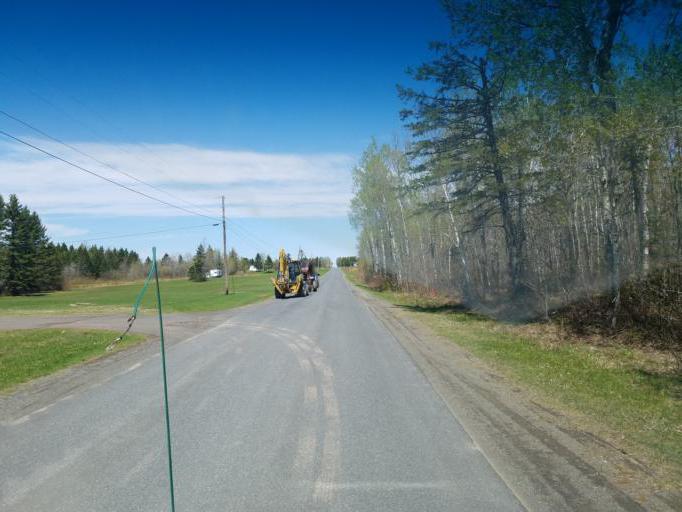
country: US
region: Maine
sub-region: Aroostook County
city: Caribou
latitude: 46.8448
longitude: -68.0703
